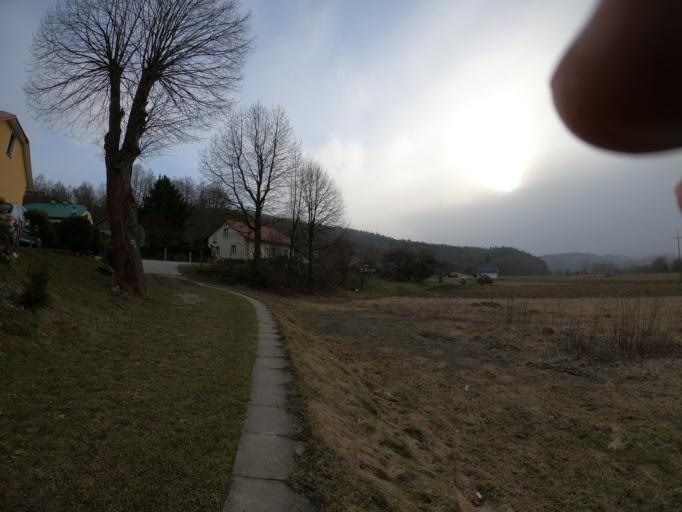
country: PL
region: Subcarpathian Voivodeship
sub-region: Powiat strzyzowski
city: Wisniowa
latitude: 49.8589
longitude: 21.6424
